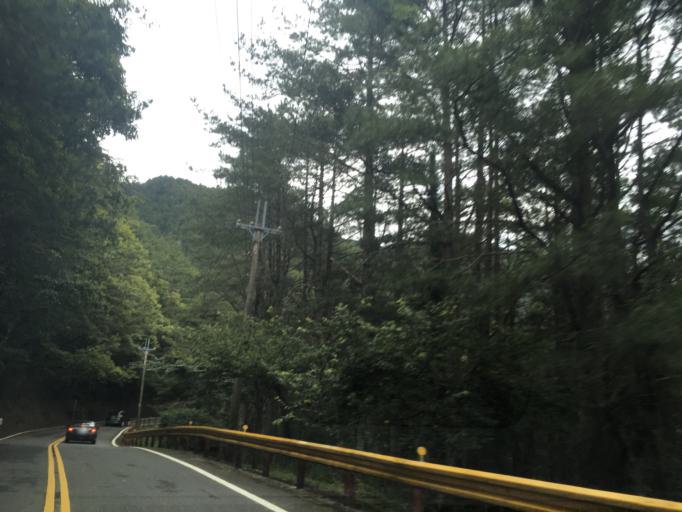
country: TW
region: Taiwan
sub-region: Hualien
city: Hualian
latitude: 24.1864
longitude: 121.3312
